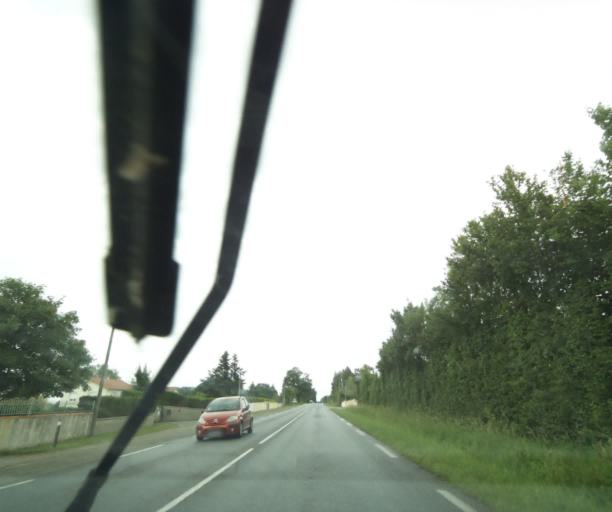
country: FR
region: Poitou-Charentes
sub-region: Departement des Deux-Sevres
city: Viennay
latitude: 46.6756
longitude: -0.2450
